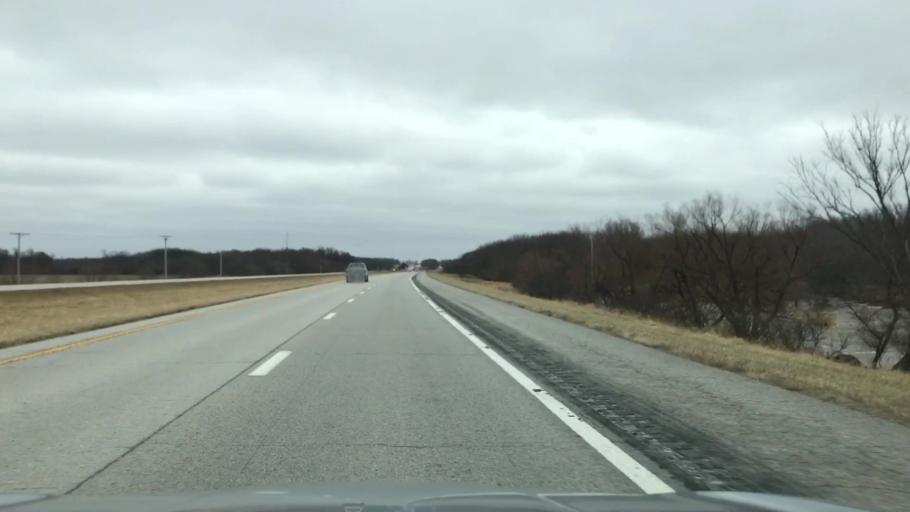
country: US
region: Missouri
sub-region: Linn County
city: Linneus
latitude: 39.7775
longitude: -93.3322
